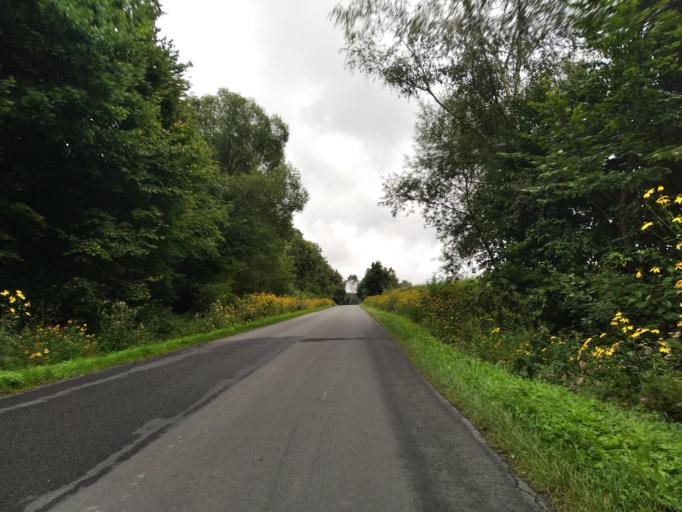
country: PL
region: Subcarpathian Voivodeship
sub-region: Powiat brzozowski
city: Nozdrzec
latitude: 49.7259
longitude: 22.2846
